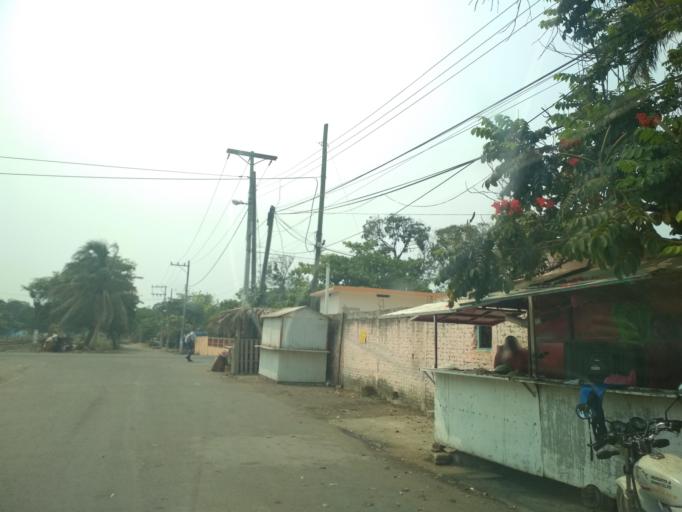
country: MX
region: Veracruz
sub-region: Veracruz
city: Delfino Victoria (Santa Fe)
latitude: 19.2053
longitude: -96.2743
